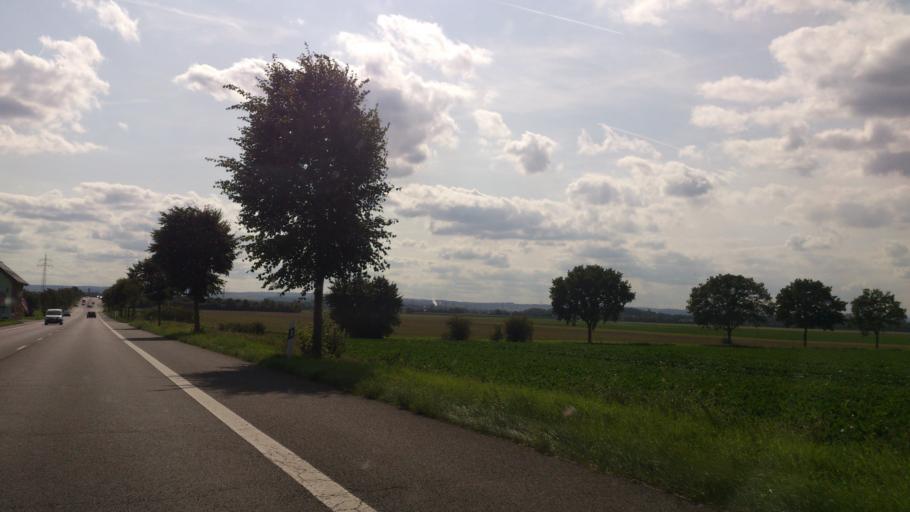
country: DE
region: North Rhine-Westphalia
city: Zulpich
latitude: 50.7182
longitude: 6.6862
